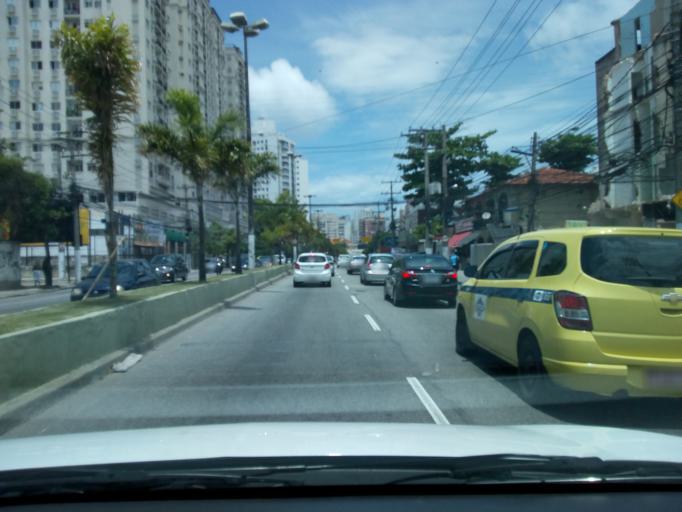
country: BR
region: Rio de Janeiro
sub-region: Niteroi
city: Niteroi
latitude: -22.8958
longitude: -43.1126
